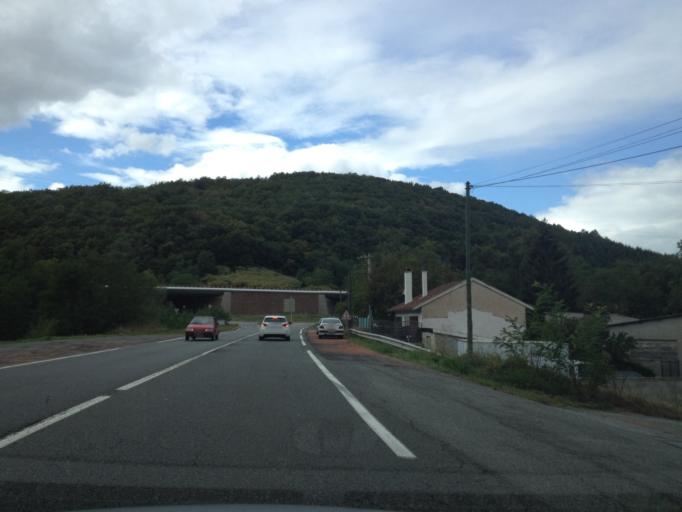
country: FR
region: Rhone-Alpes
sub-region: Departement de la Loire
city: Perreux
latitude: 45.9654
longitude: 4.1373
